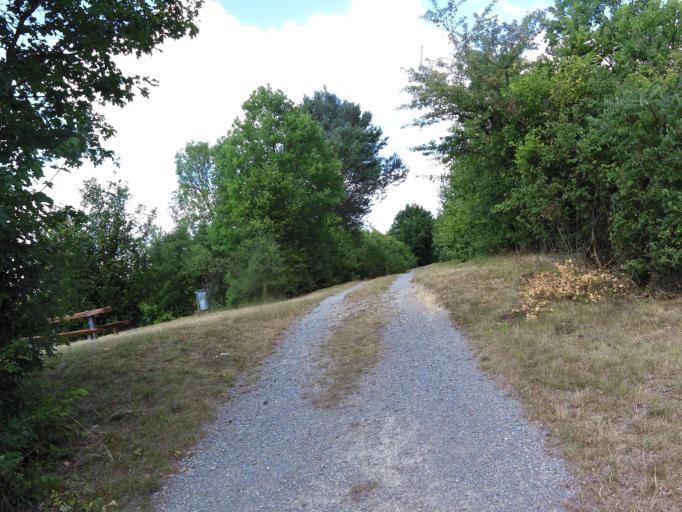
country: DE
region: Bavaria
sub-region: Regierungsbezirk Unterfranken
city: Gerbrunn
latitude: 49.7765
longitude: 10.0012
